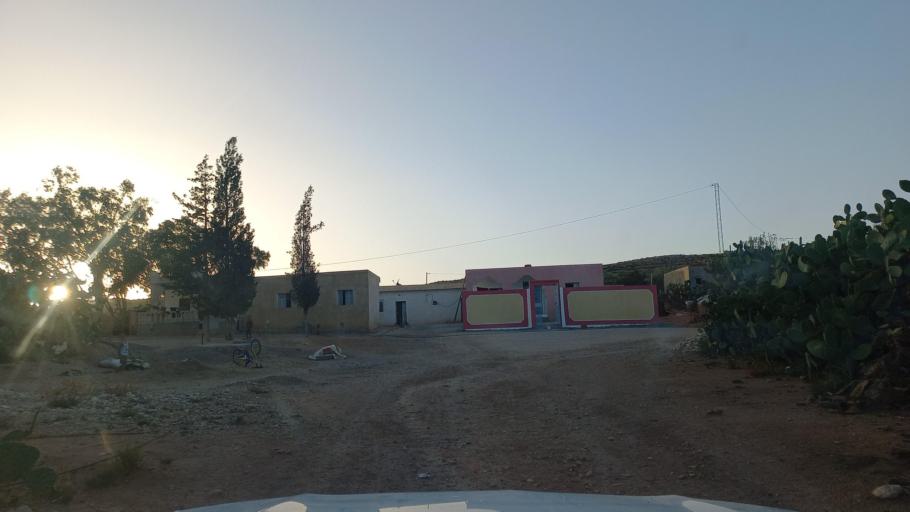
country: TN
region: Al Qasrayn
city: Sbiba
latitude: 35.3745
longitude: 9.0089
